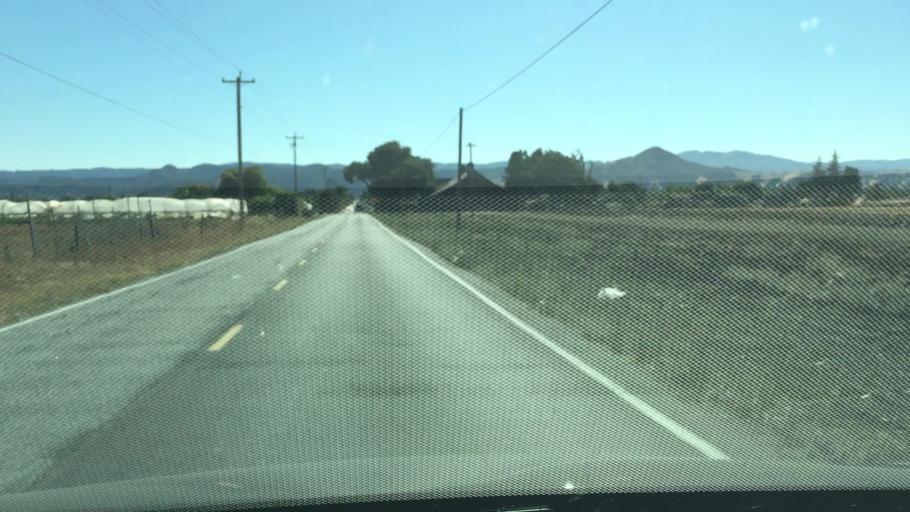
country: US
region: California
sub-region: Santa Clara County
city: San Martin
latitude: 37.1277
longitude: -121.6042
